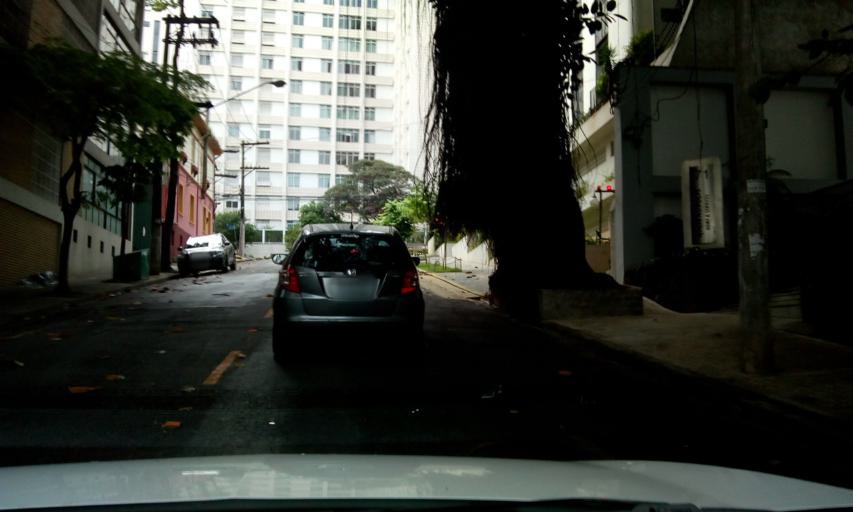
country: BR
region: Sao Paulo
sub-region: Sao Paulo
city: Sao Paulo
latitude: -23.5359
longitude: -46.6615
